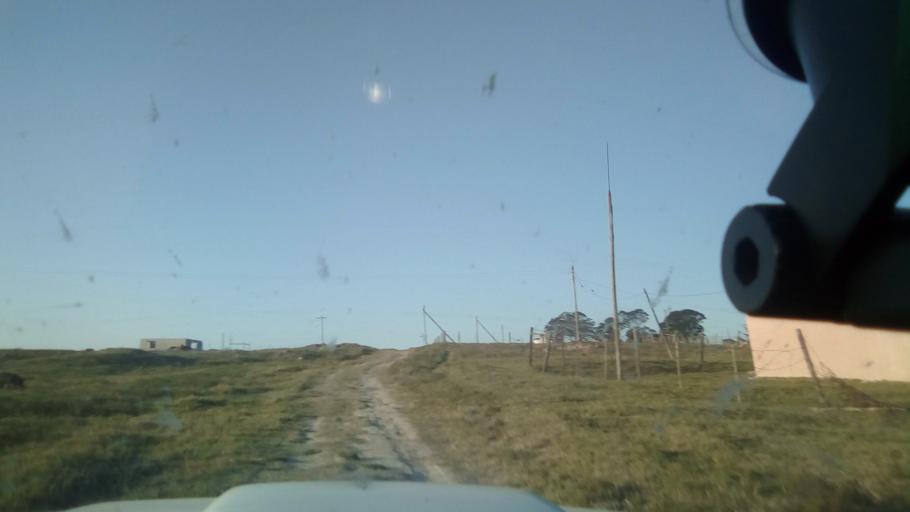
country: ZA
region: Eastern Cape
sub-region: Buffalo City Metropolitan Municipality
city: Bhisho
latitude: -32.9734
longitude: 27.2912
